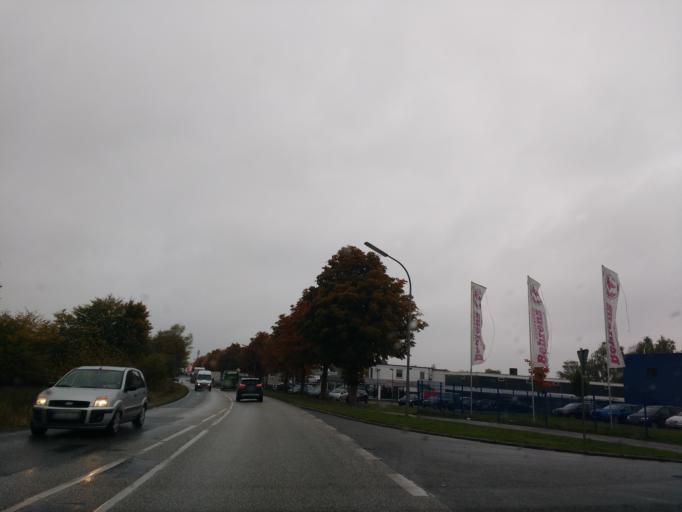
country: DE
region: Schleswig-Holstein
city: Eutin
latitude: 54.1235
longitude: 10.6336
